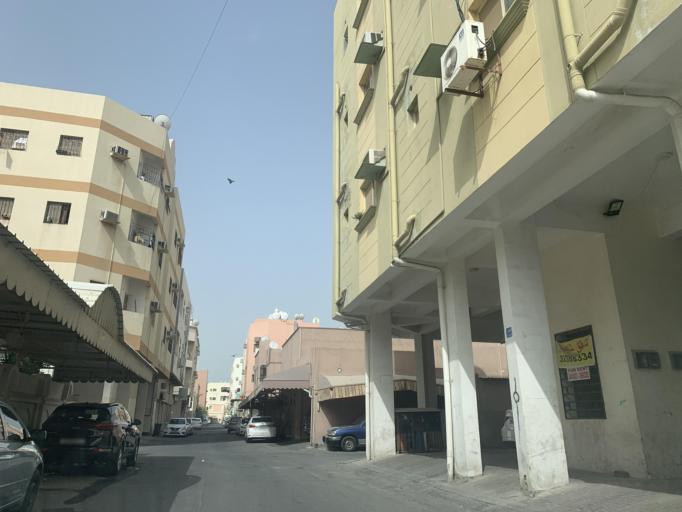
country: BH
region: Northern
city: Ar Rifa'
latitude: 26.1259
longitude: 50.5695
